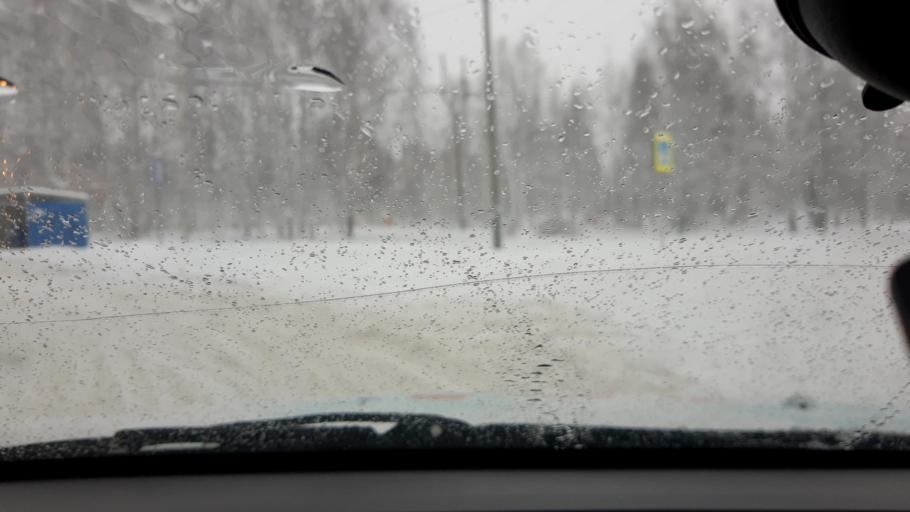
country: RU
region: Nizjnij Novgorod
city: Kstovo
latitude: 56.1593
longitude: 44.2190
